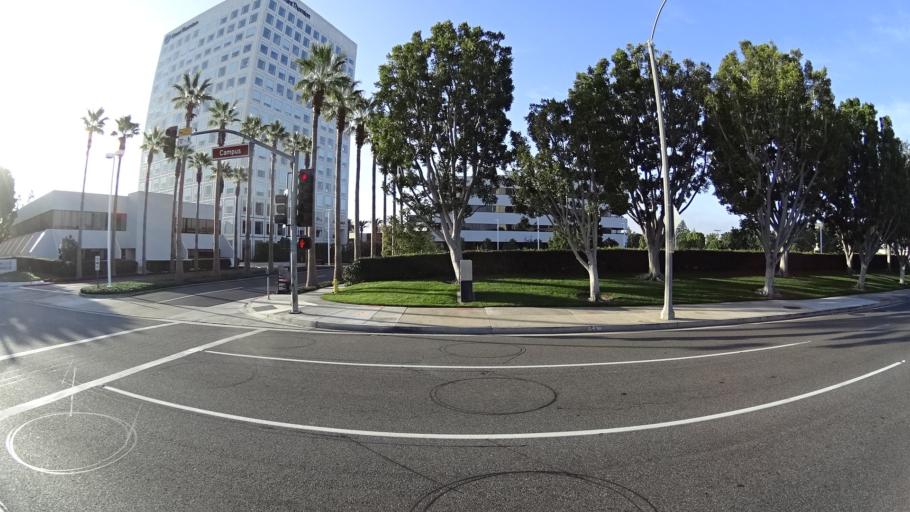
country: US
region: California
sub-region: Orange County
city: Irvine
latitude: 33.6716
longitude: -117.8623
